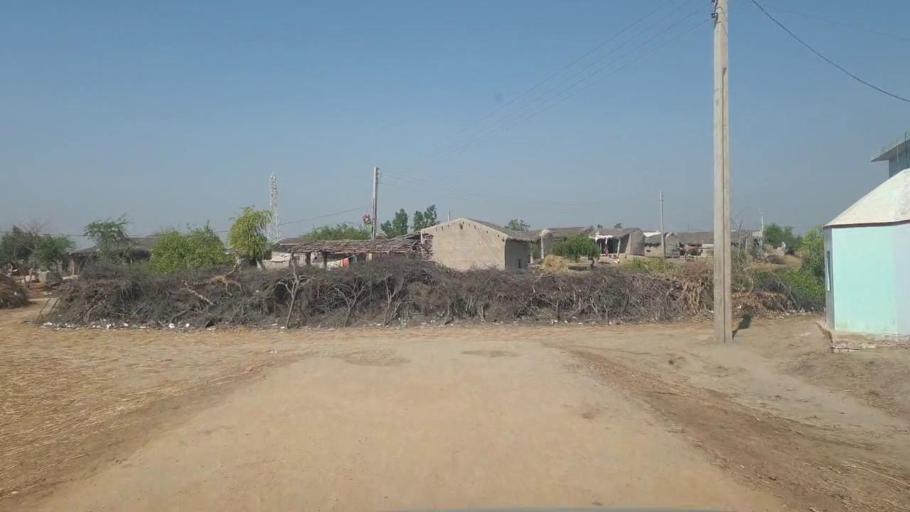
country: PK
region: Sindh
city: Badin
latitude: 24.6812
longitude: 68.9001
